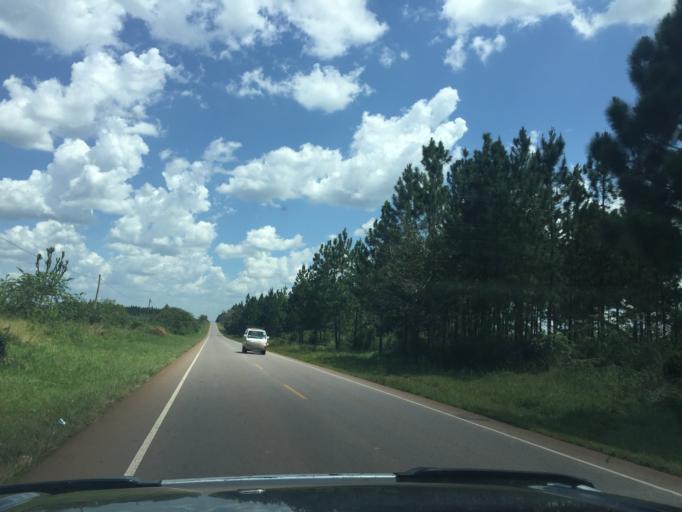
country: UG
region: Central Region
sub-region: Nakasongola District
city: Nakasongola
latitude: 1.3815
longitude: 32.3375
